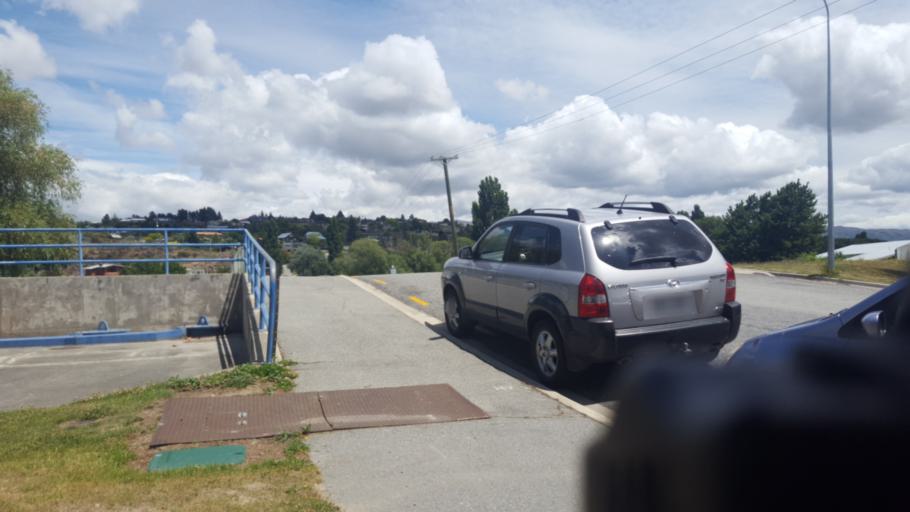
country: NZ
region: Otago
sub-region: Queenstown-Lakes District
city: Wanaka
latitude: -45.2567
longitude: 169.3895
